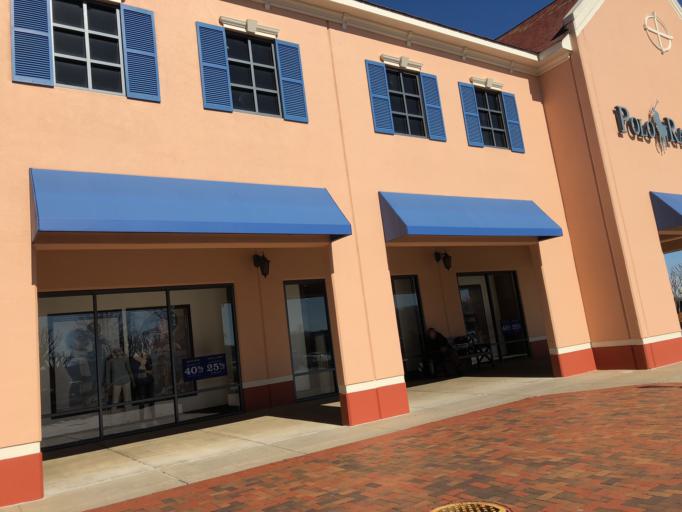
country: US
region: Georgia
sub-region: Dawson County
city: Dawsonville
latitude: 34.3588
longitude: -84.0466
